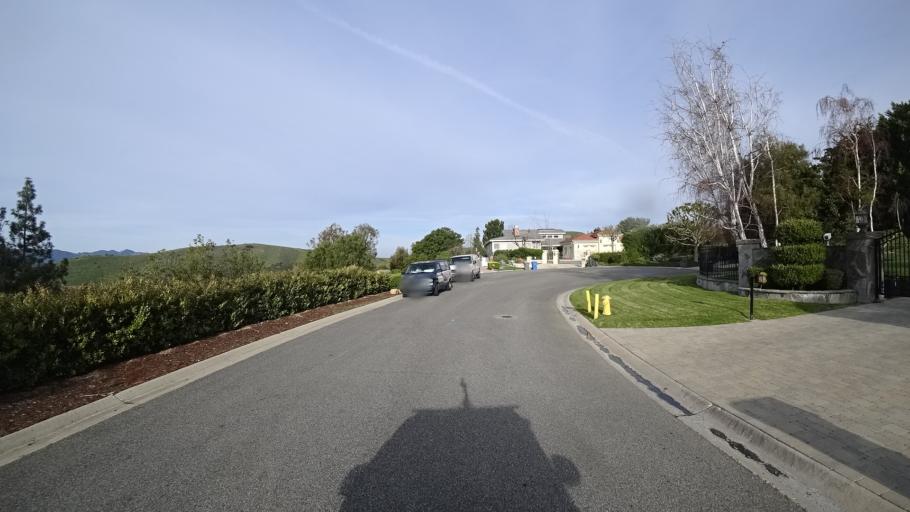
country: US
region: California
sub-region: Ventura County
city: Thousand Oaks
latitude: 34.1875
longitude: -118.8148
